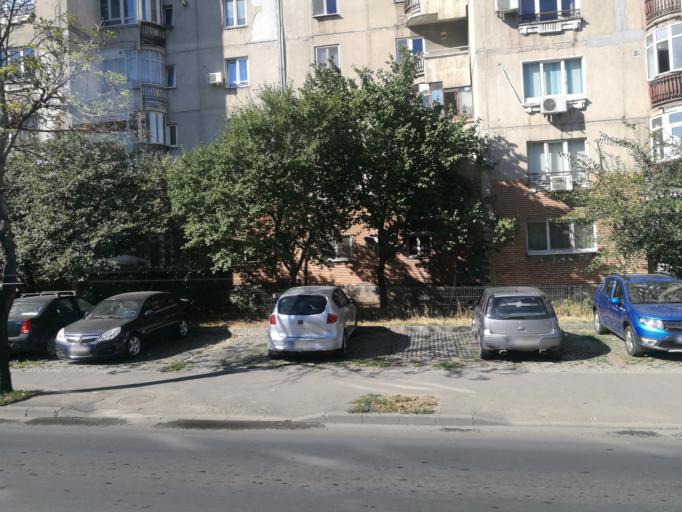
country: RO
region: Ilfov
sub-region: Comuna Chiajna
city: Rosu
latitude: 44.4411
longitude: 26.0352
